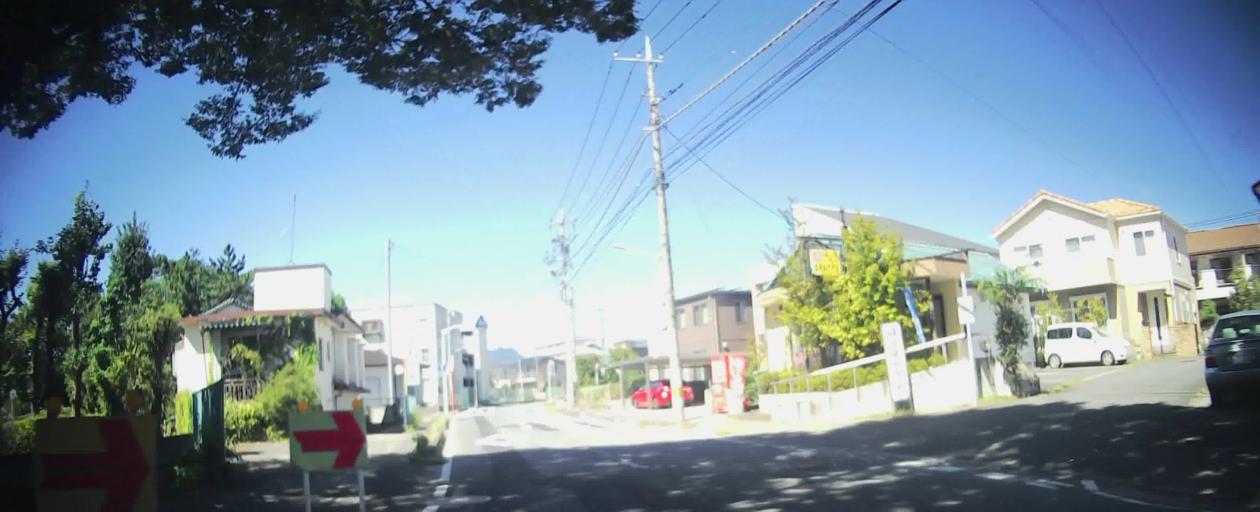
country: JP
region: Gunma
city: Maebashi-shi
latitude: 36.3984
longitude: 139.0583
